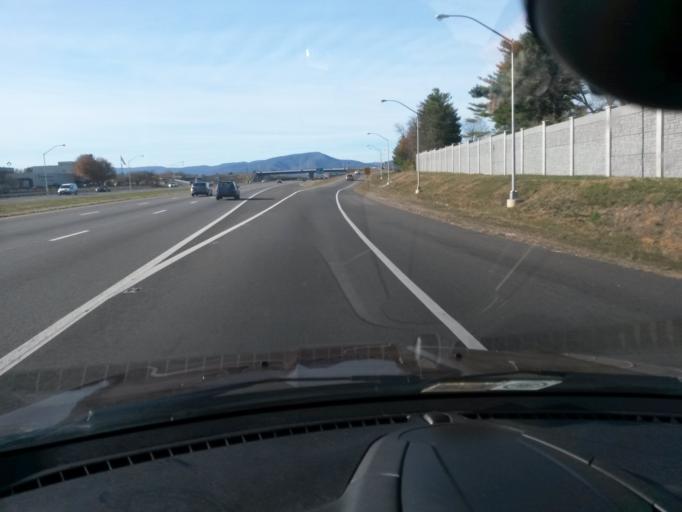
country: US
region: Virginia
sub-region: City of Roanoke
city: Roanoke
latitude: 37.2955
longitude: -79.9542
